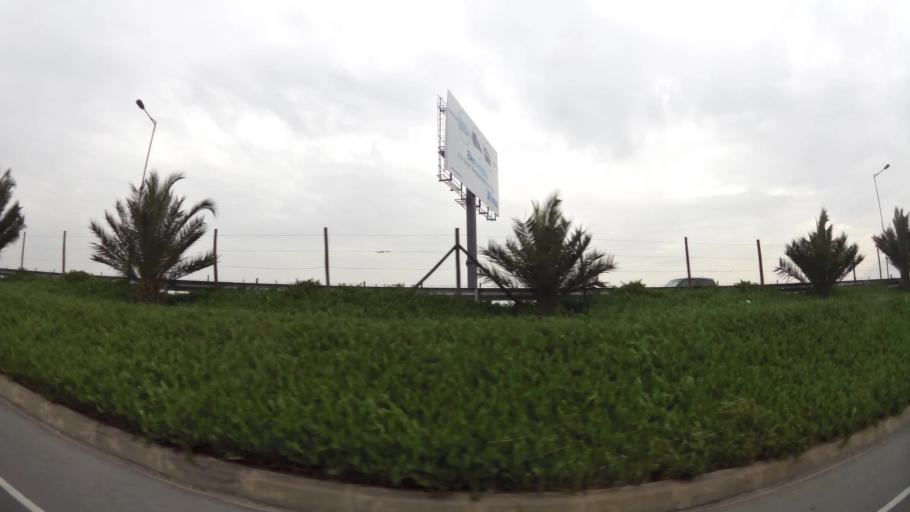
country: CL
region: Santiago Metropolitan
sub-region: Provincia de Santiago
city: Lo Prado
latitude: -33.4234
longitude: -70.7867
